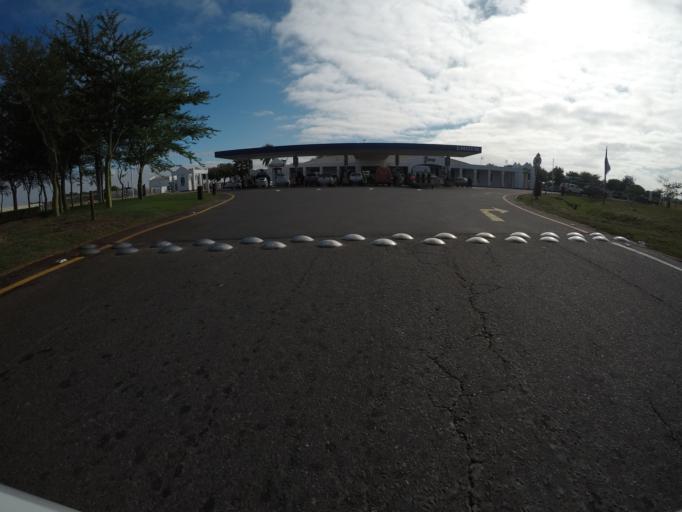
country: ZA
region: Western Cape
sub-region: City of Cape Town
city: Kraaifontein
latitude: -33.8273
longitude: 18.7625
